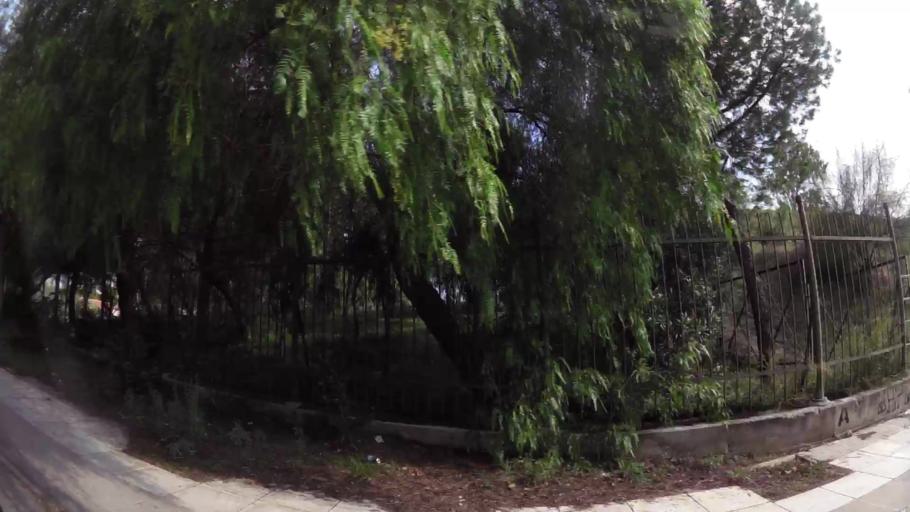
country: GR
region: Attica
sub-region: Nomarchia Athinas
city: Athens
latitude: 37.9674
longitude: 23.7149
